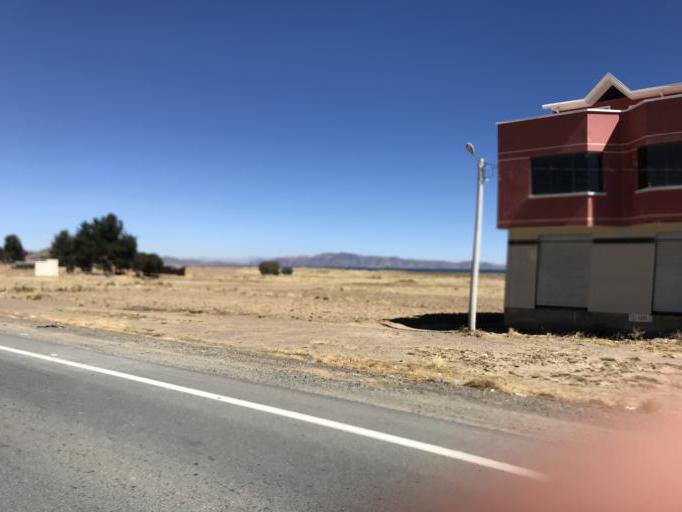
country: BO
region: La Paz
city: Huarina
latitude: -16.2024
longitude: -68.5970
